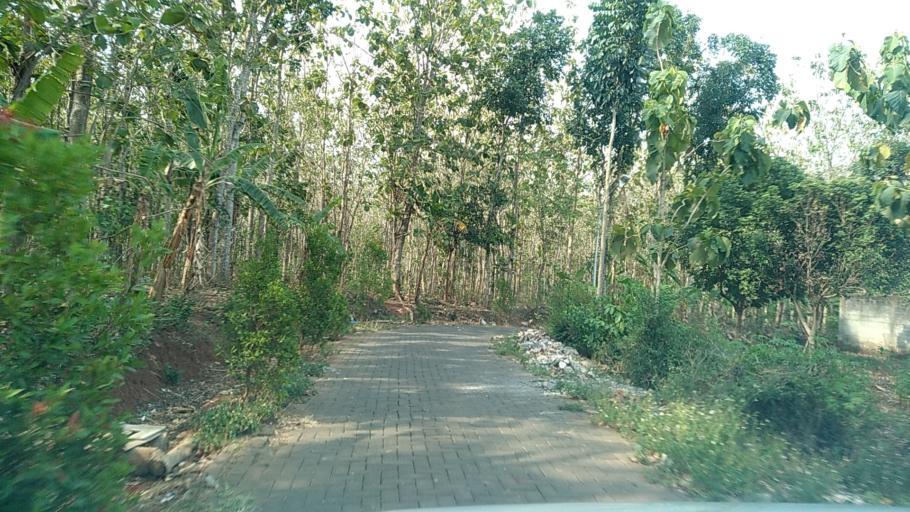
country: ID
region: Central Java
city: Semarang
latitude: -7.0464
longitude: 110.3109
